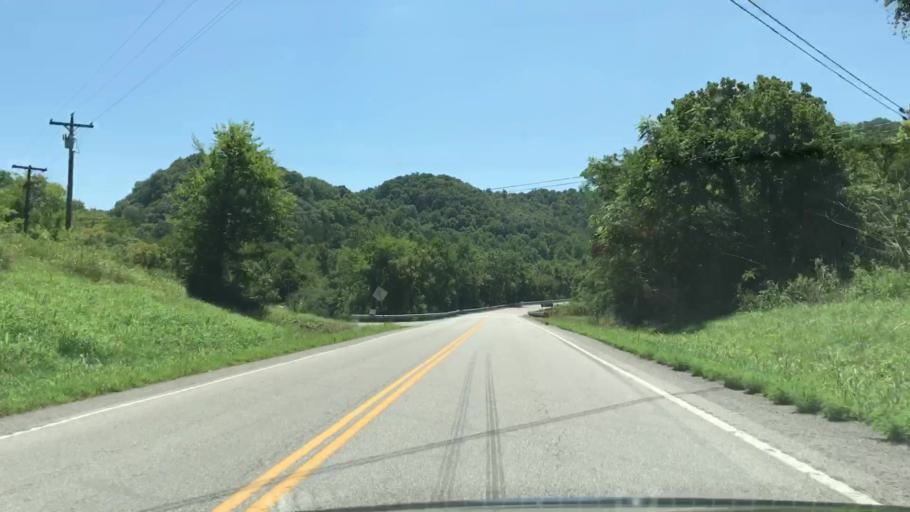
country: US
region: Tennessee
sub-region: Clay County
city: Celina
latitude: 36.4861
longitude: -85.5617
